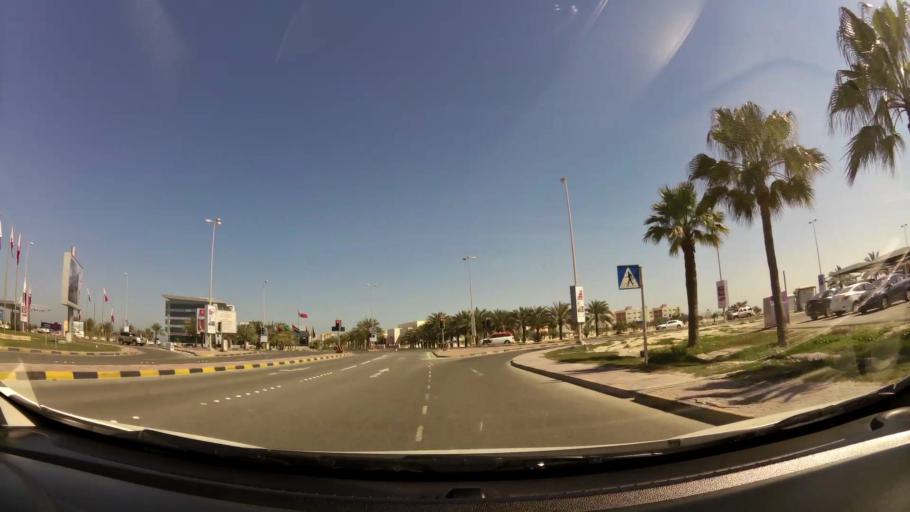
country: BH
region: Muharraq
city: Al Hadd
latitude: 26.2784
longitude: 50.6625
